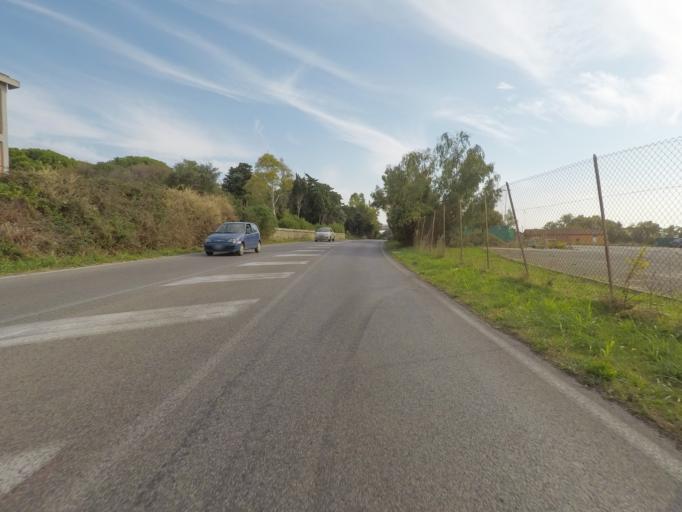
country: IT
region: Latium
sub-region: Citta metropolitana di Roma Capitale
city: Civitavecchia
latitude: 42.0607
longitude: 11.8167
